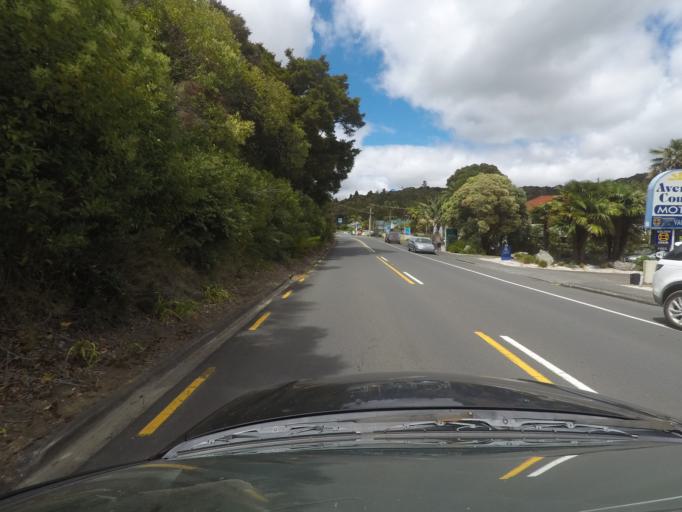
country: NZ
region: Northland
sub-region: Far North District
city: Paihia
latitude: -35.2864
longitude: 174.0964
